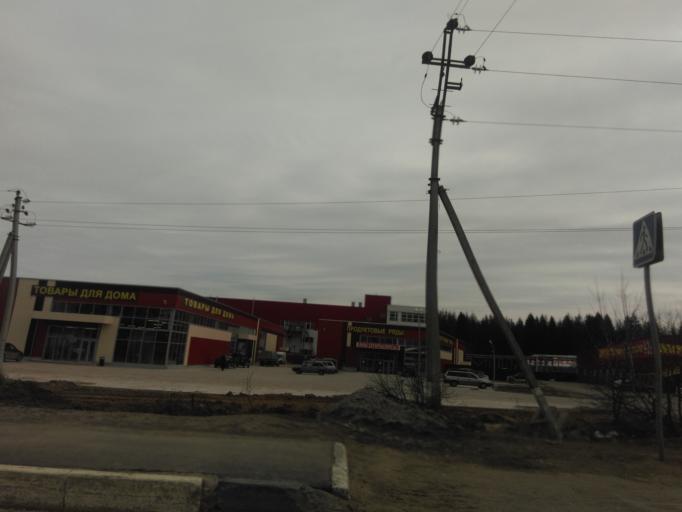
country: RU
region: Moskovskaya
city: Tuchkovo
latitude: 55.6067
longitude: 36.4928
